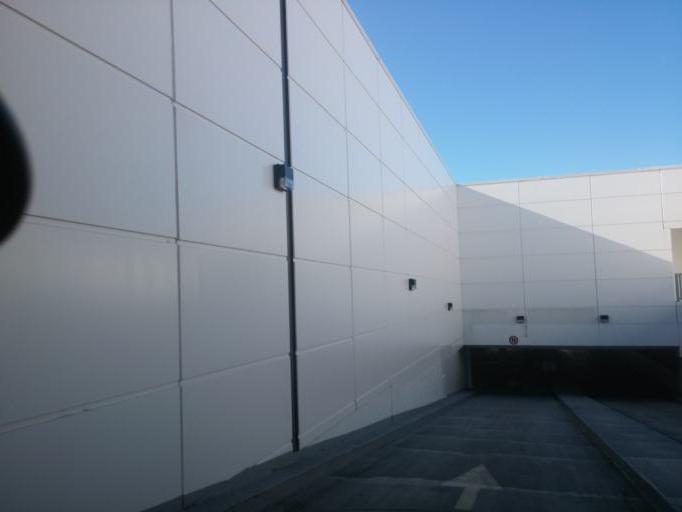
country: NZ
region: Wellington
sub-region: Wellington City
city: Wellington
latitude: -41.3077
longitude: 174.7766
